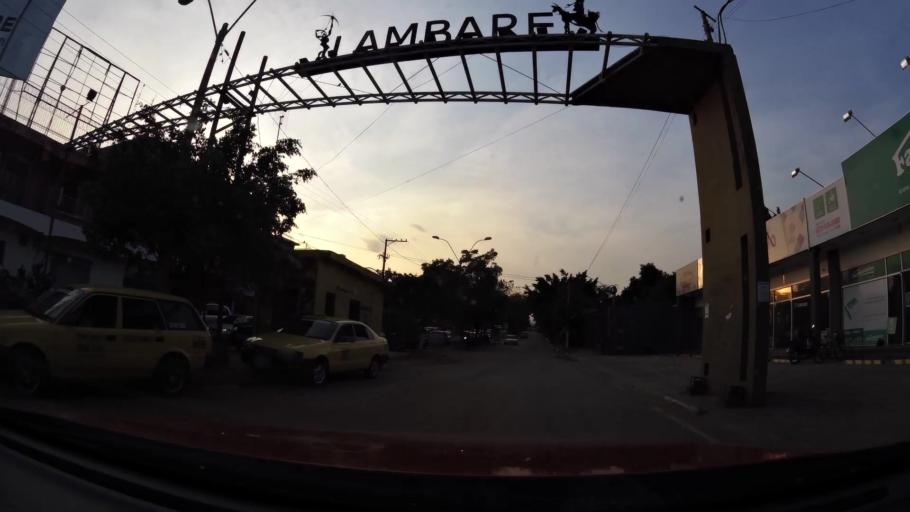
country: PY
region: Central
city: Villa Elisa
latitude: -25.3577
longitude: -57.5959
